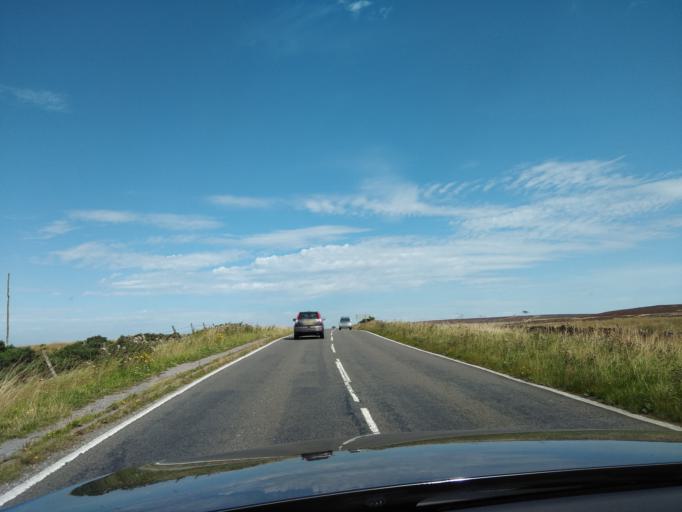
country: GB
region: England
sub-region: Derbyshire
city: Hathersage
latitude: 53.3077
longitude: -1.5989
